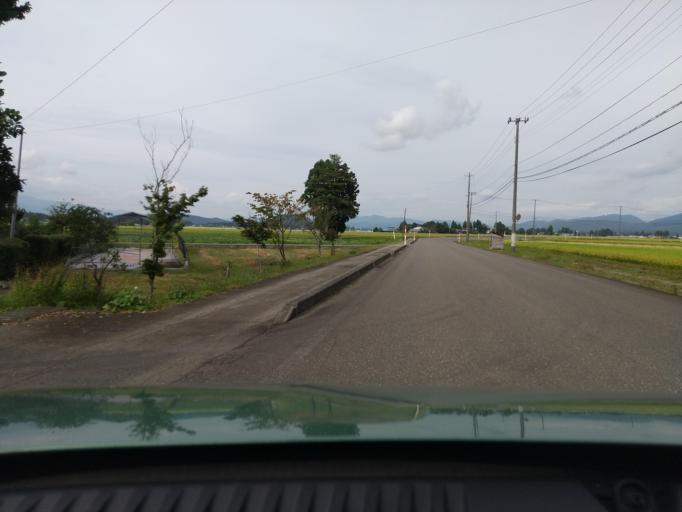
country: JP
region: Akita
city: Kakunodatemachi
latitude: 39.5516
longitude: 140.5689
